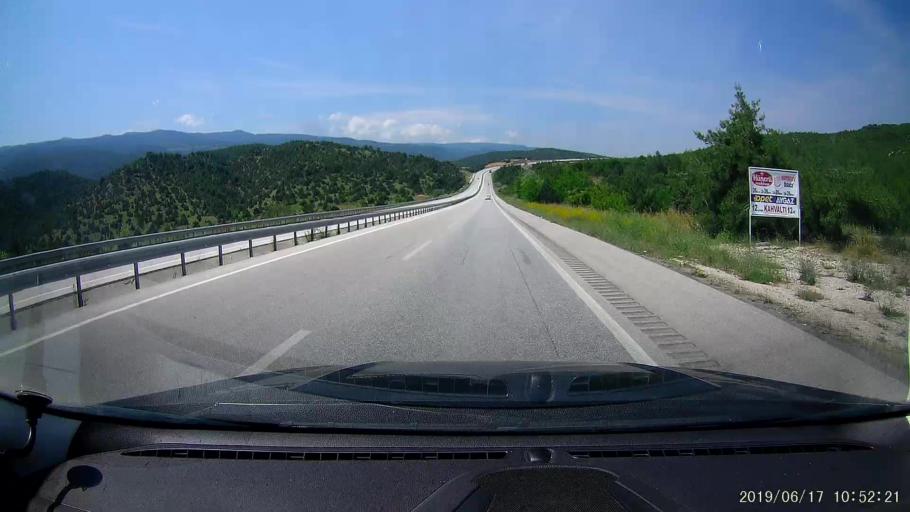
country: TR
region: Corum
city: Hacihamza
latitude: 41.0906
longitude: 34.3436
